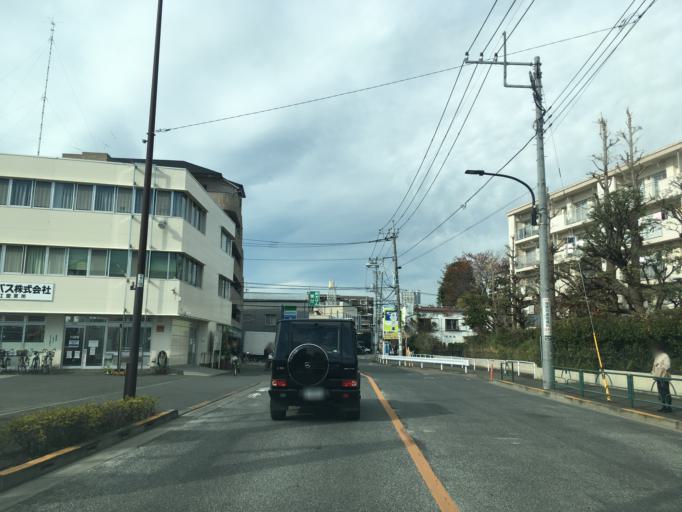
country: JP
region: Tokyo
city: Chofugaoka
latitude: 35.6429
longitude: 139.5674
